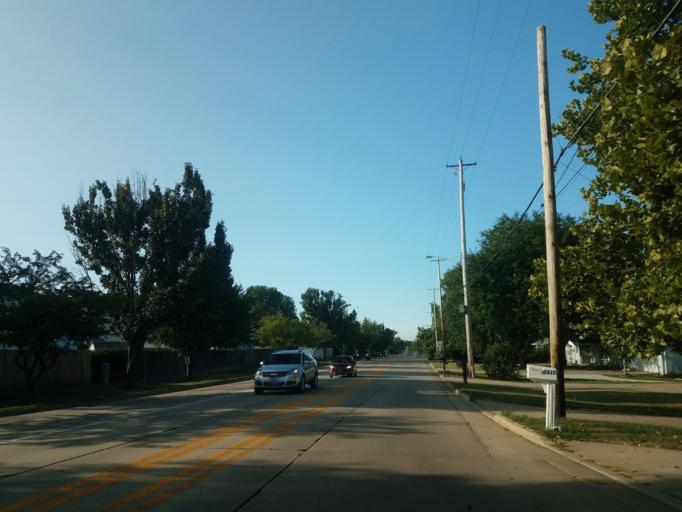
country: US
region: Illinois
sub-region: McLean County
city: Normal
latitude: 40.5314
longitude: -88.9833
